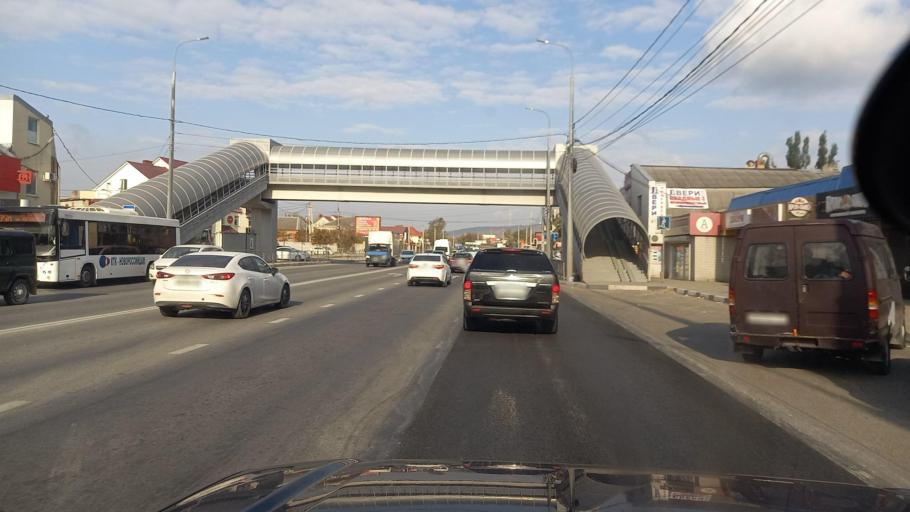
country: RU
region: Krasnodarskiy
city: Gayduk
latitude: 44.7615
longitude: 37.7203
